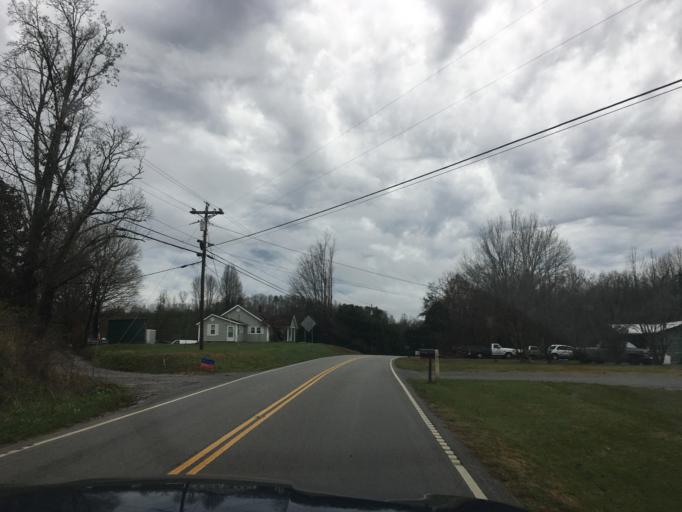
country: US
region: Tennessee
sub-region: Monroe County
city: Madisonville
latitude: 35.3668
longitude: -84.3209
